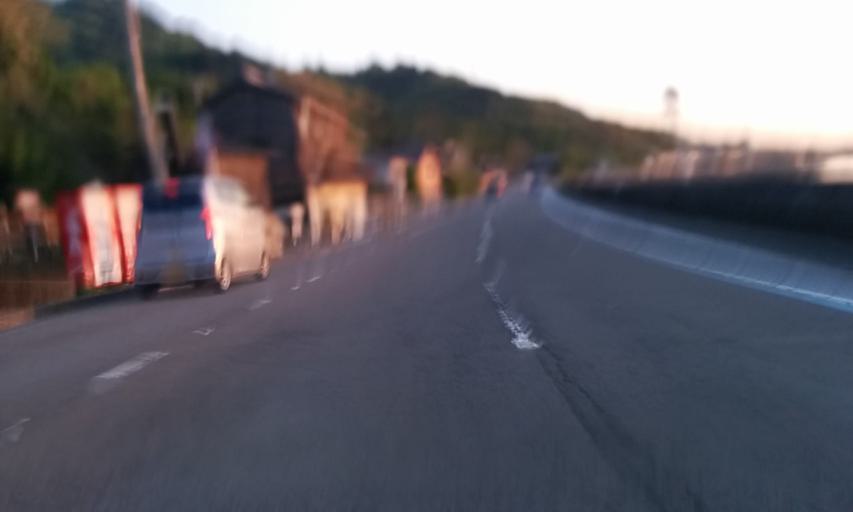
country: JP
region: Ehime
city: Iyo
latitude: 33.6805
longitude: 132.6282
